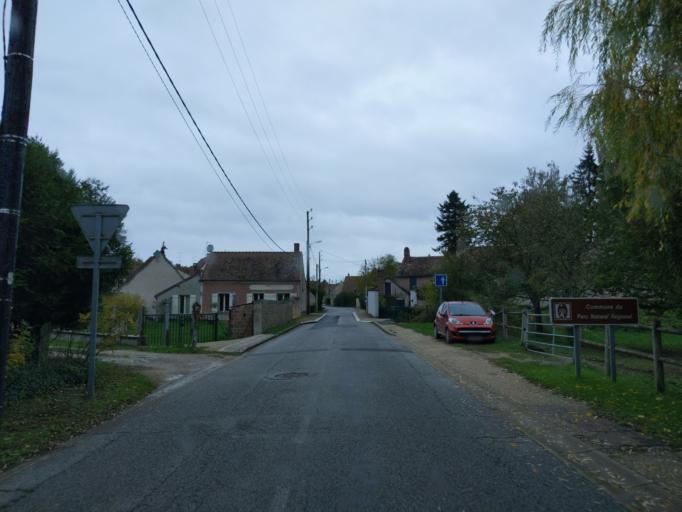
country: FR
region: Ile-de-France
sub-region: Departement des Yvelines
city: Bullion
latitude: 48.6223
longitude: 1.9916
